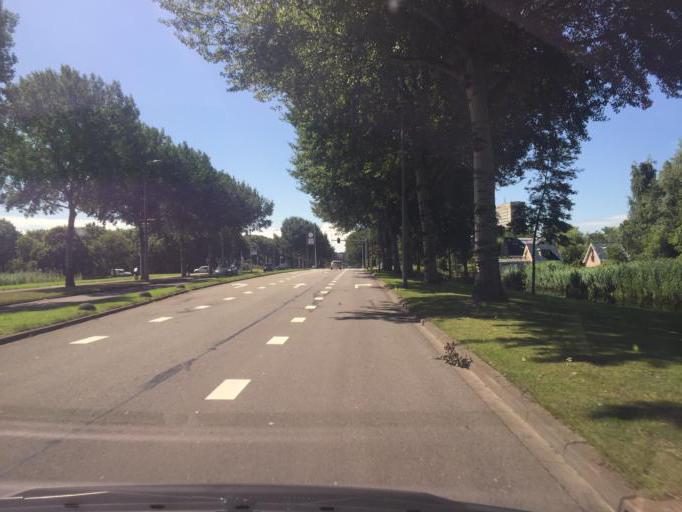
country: NL
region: South Holland
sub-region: Gemeente Rotterdam
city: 's-Gravenland
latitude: 51.9236
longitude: 4.5322
